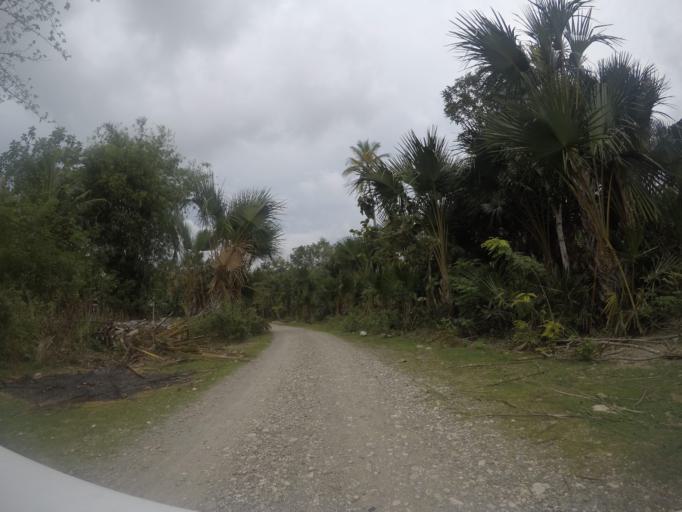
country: TL
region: Viqueque
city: Viqueque
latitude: -8.8560
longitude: 126.3682
